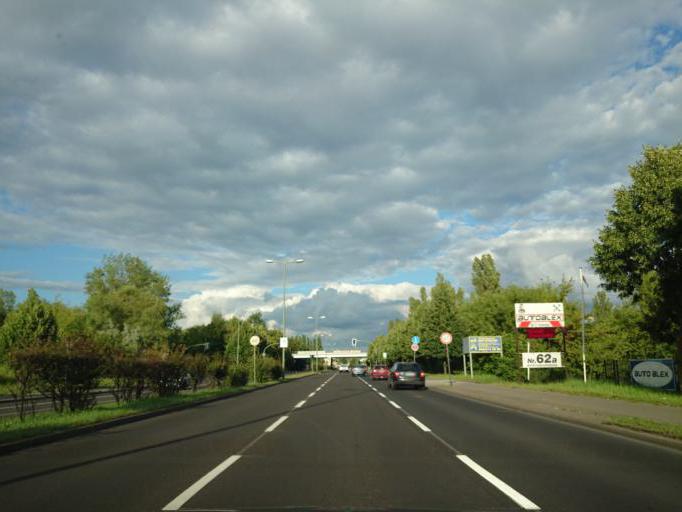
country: DE
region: Berlin
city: Biesdorf
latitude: 52.5099
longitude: 13.5406
